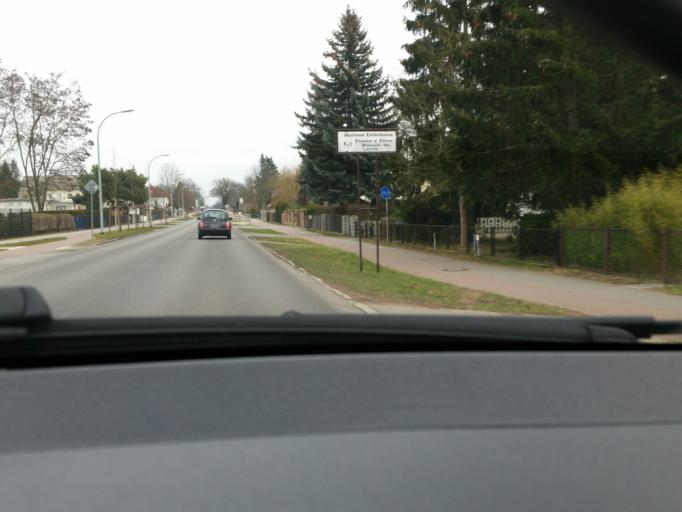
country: DE
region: Brandenburg
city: Teltow
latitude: 52.3936
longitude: 13.2864
